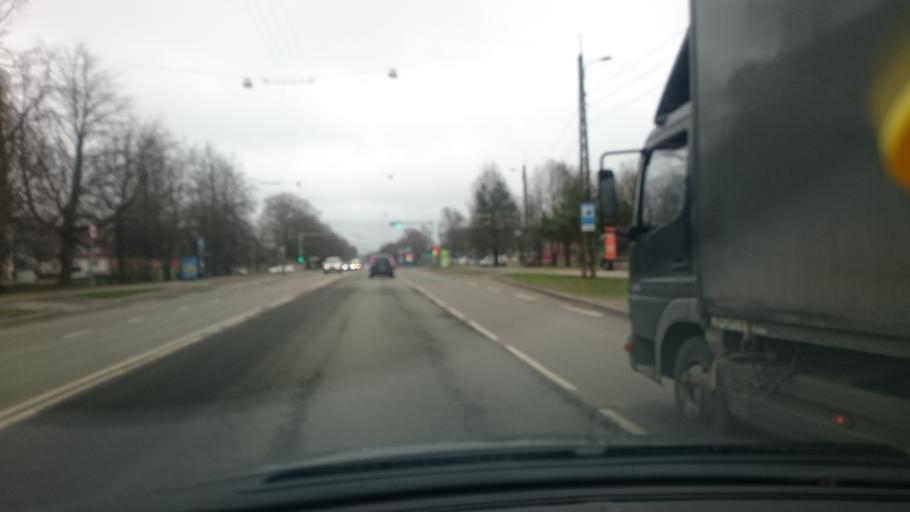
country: EE
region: Harju
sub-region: Tallinna linn
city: Tallinn
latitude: 59.4403
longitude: 24.7071
